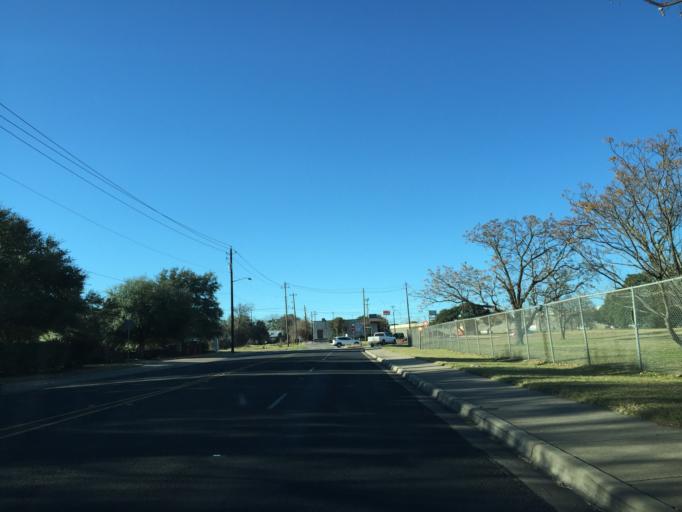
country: US
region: Texas
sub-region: Williamson County
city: Jollyville
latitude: 30.4199
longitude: -97.7447
